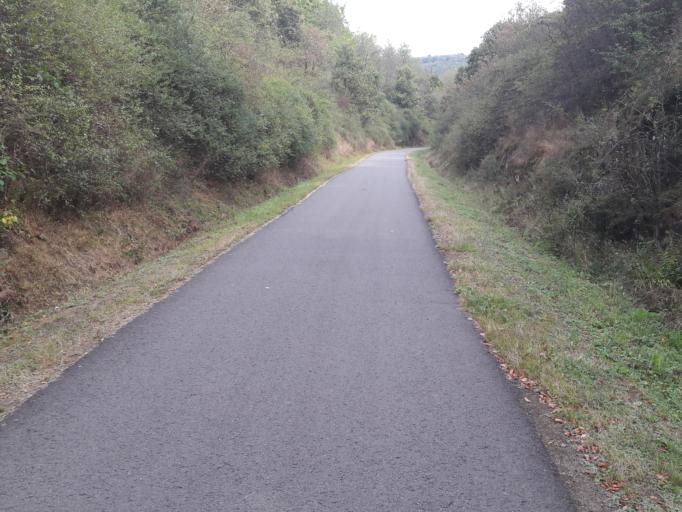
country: DE
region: Saarland
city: Oberthal
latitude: 49.5092
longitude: 7.0742
